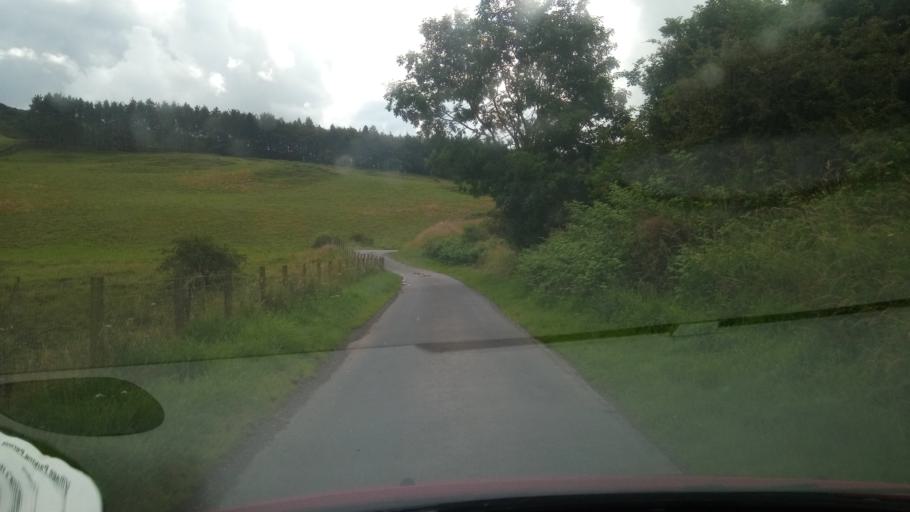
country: GB
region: Scotland
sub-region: The Scottish Borders
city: Hawick
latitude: 55.4125
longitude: -2.7591
